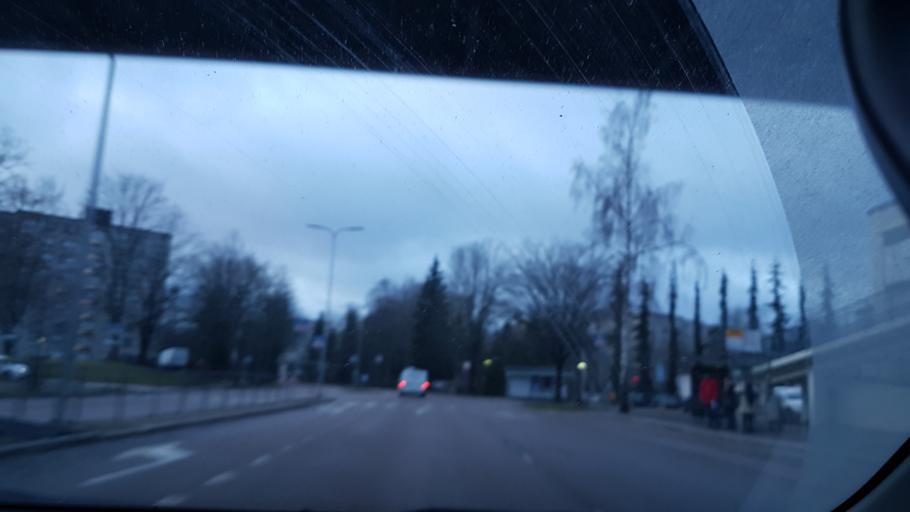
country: FI
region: Uusimaa
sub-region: Helsinki
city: Vantaa
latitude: 60.2781
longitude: 25.1061
